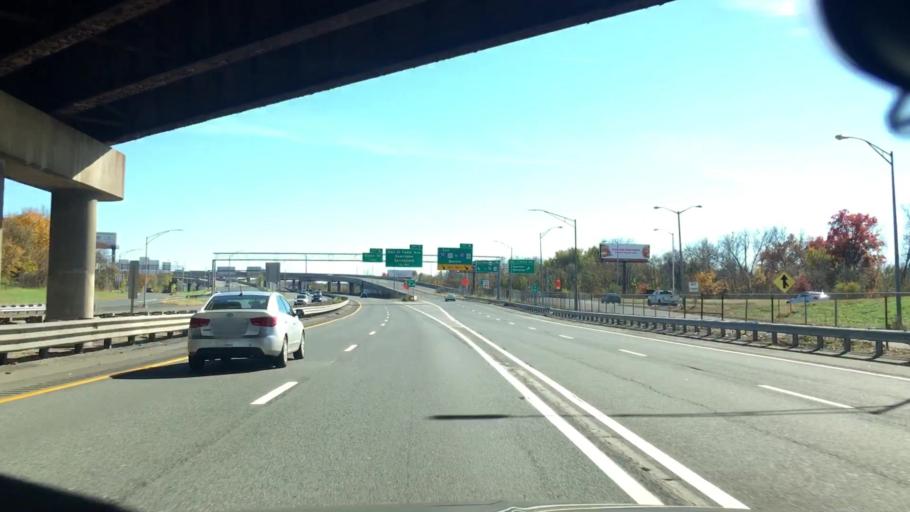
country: US
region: Massachusetts
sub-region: Hampden County
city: West Springfield
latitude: 42.1113
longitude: -72.6064
